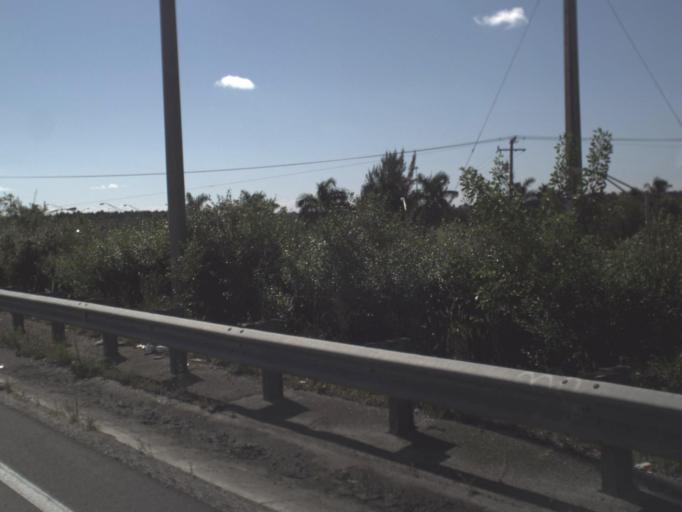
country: US
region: Florida
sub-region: Miami-Dade County
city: Richmond Heights
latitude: 25.6284
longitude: -80.3807
